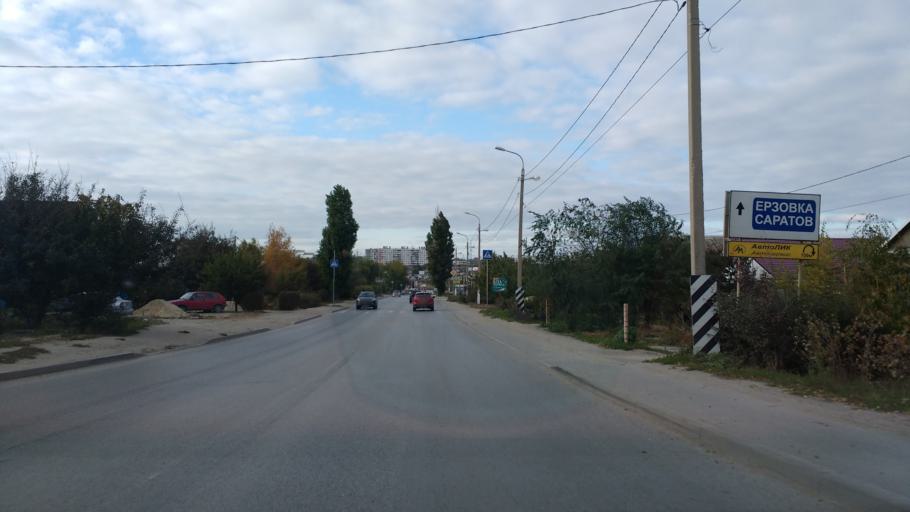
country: RU
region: Volgograd
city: Volgograd
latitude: 48.7708
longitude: 44.5245
